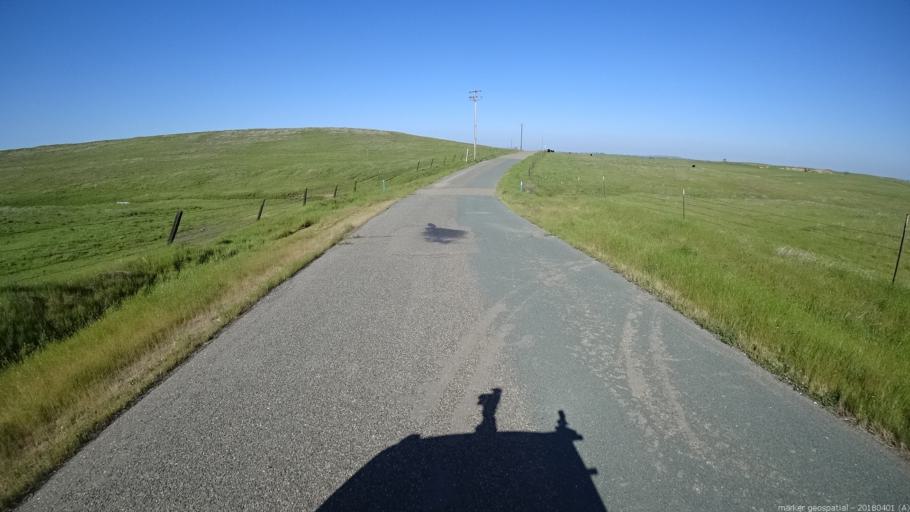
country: US
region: California
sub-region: Sacramento County
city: Rancho Murieta
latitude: 38.4642
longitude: -121.1160
